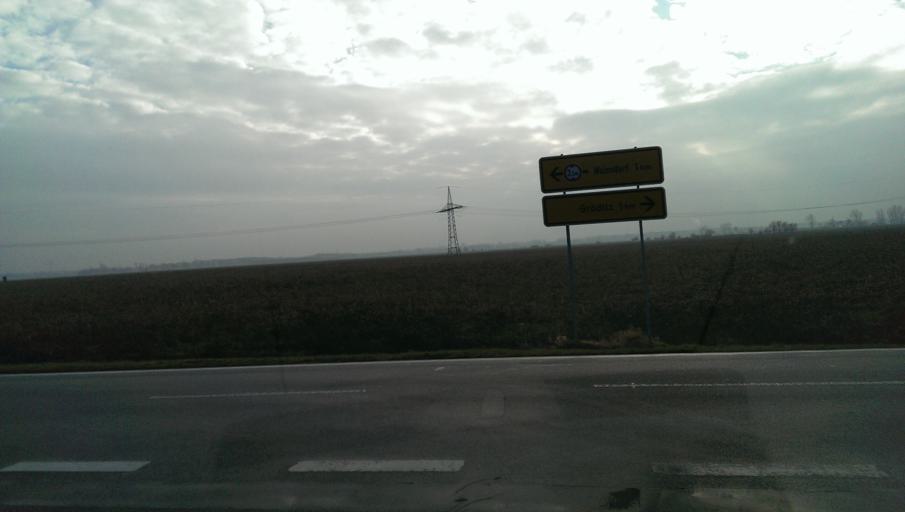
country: DE
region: Brandenburg
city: Merzdorf
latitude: 51.4120
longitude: 13.4756
